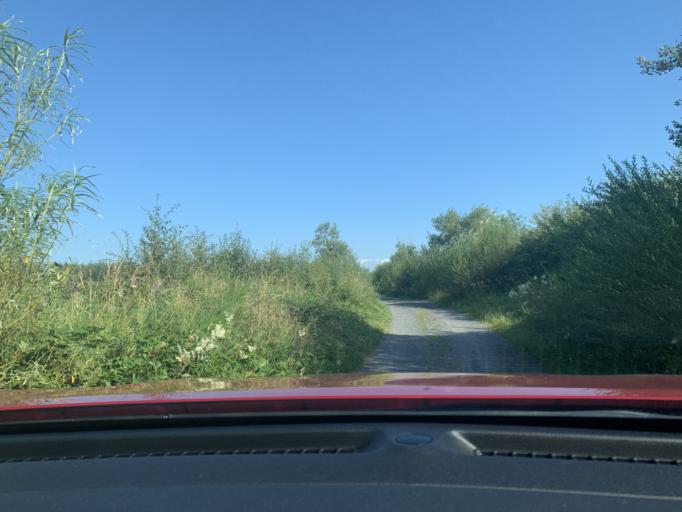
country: IE
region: Connaught
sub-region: Sligo
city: Tobercurry
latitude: 54.0648
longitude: -8.7877
